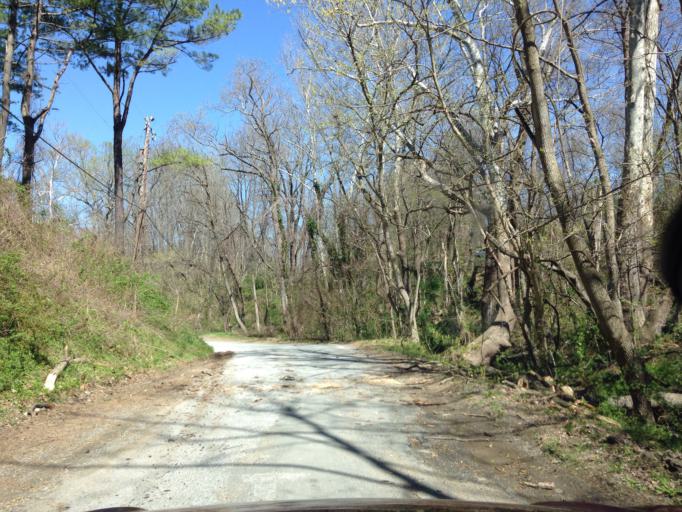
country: US
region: Maryland
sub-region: Frederick County
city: Brunswick
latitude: 39.2983
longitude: -77.6339
